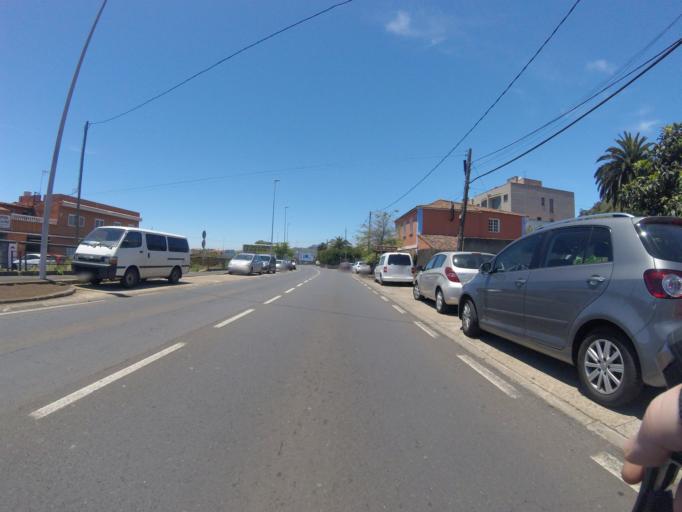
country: ES
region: Canary Islands
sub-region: Provincia de Santa Cruz de Tenerife
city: Tegueste
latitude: 28.5069
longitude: -16.3110
